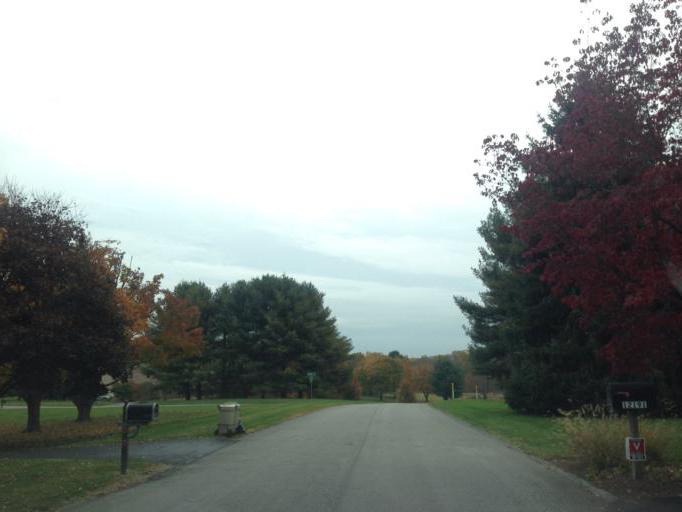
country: US
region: Maryland
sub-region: Howard County
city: Highland
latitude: 39.2728
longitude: -76.9324
